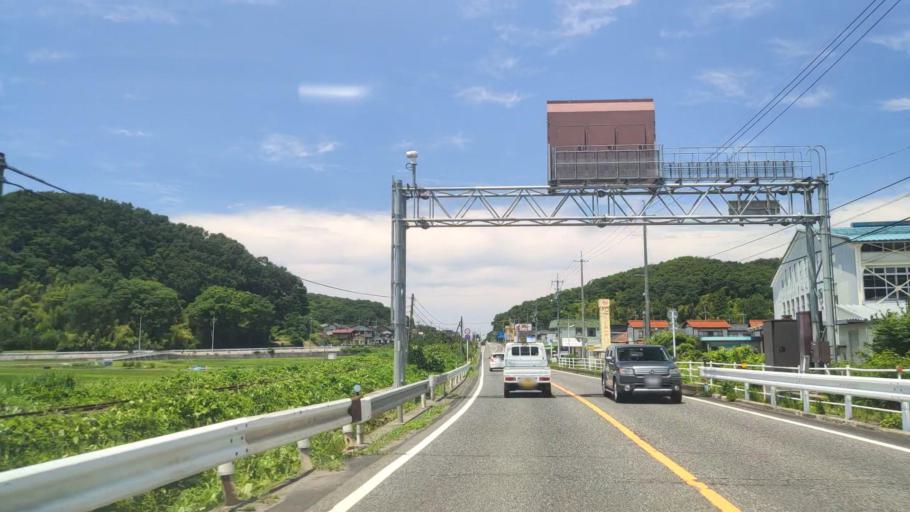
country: JP
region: Tottori
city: Tottori
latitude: 35.4244
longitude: 134.2621
